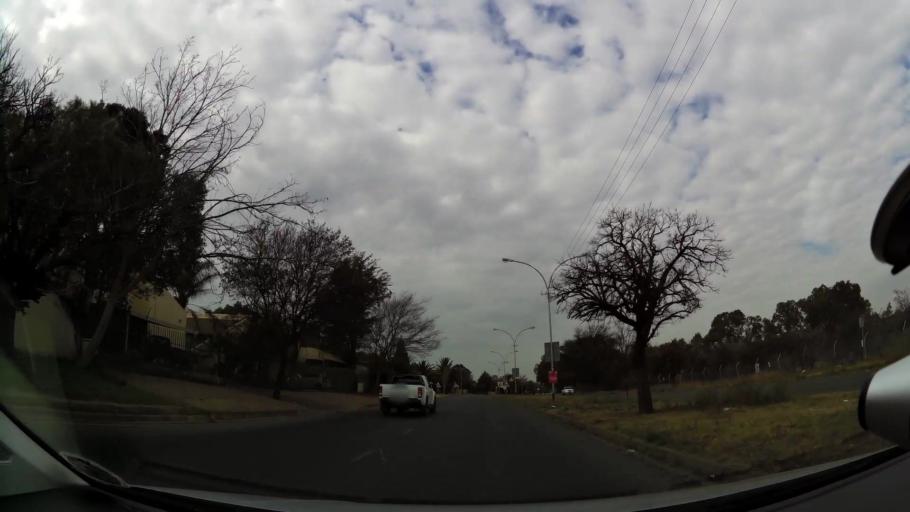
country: ZA
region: Orange Free State
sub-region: Mangaung Metropolitan Municipality
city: Bloemfontein
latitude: -29.0836
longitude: 26.2216
